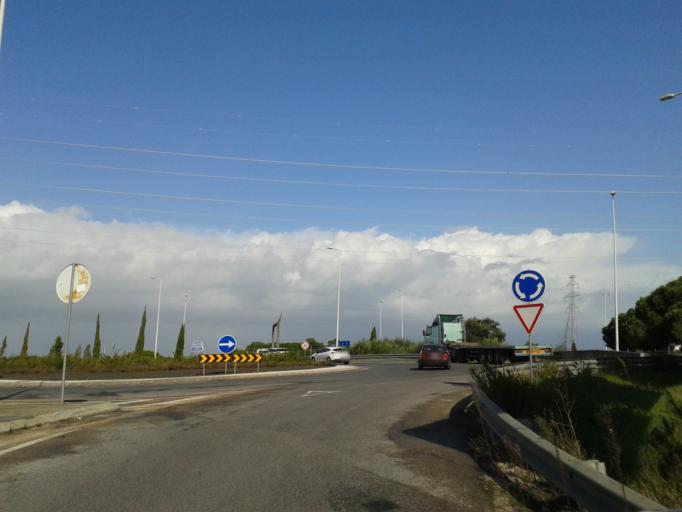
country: PT
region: Setubal
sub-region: Palmela
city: Palmela
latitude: 38.5839
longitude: -8.8902
